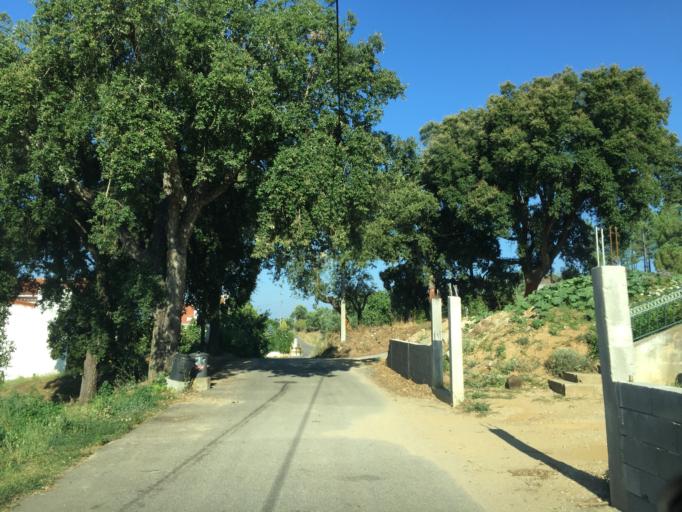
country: PT
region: Santarem
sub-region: Abrantes
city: Alferrarede
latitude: 39.5211
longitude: -8.1347
